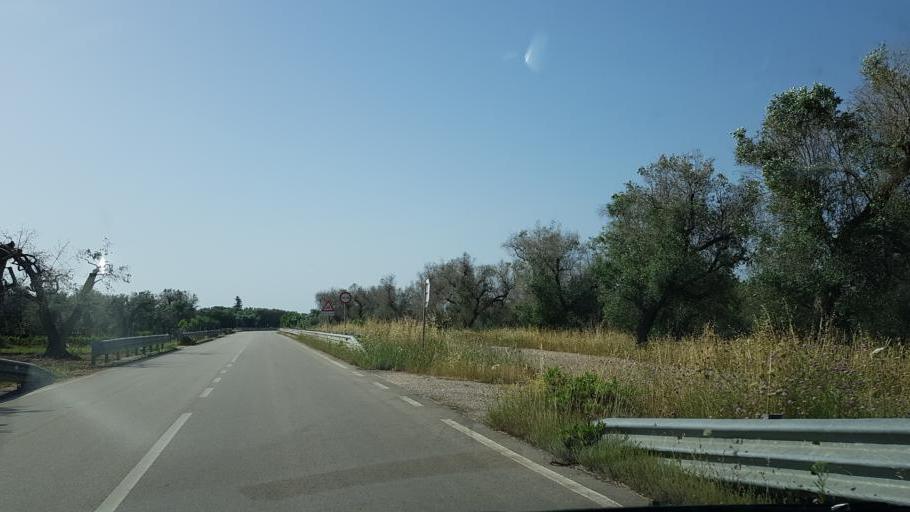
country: IT
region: Apulia
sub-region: Provincia di Brindisi
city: Mesagne
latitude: 40.4943
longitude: 17.8315
